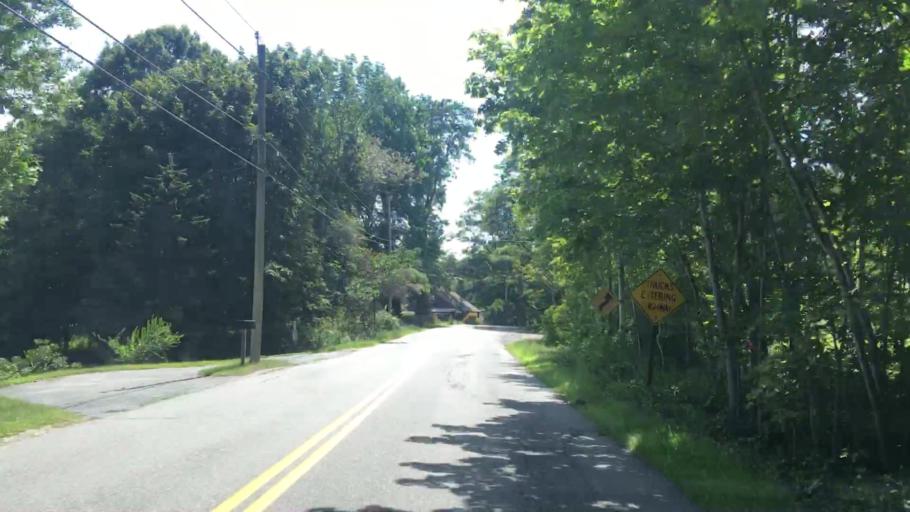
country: US
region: Maine
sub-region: Cumberland County
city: South Portland
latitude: 43.6179
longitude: -70.2577
